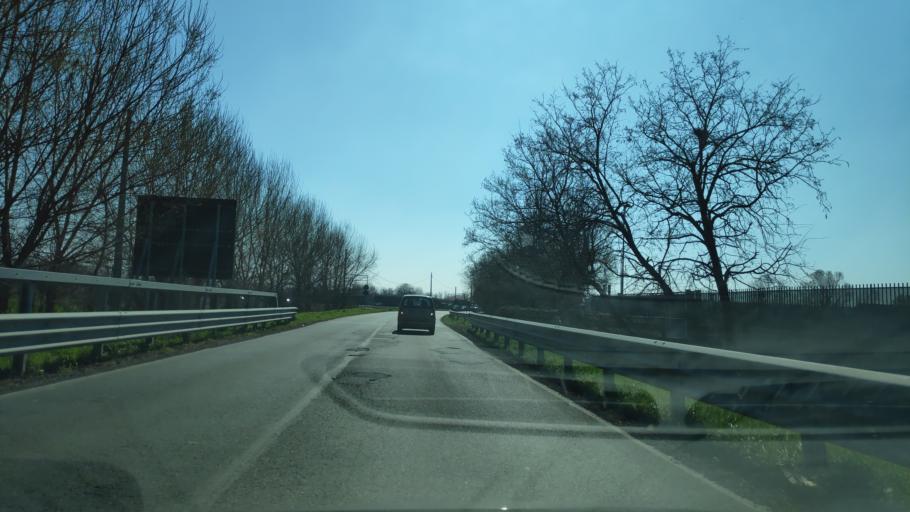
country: IT
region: Lombardy
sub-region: Citta metropolitana di Milano
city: Premenugo
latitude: 45.4814
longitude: 9.3804
